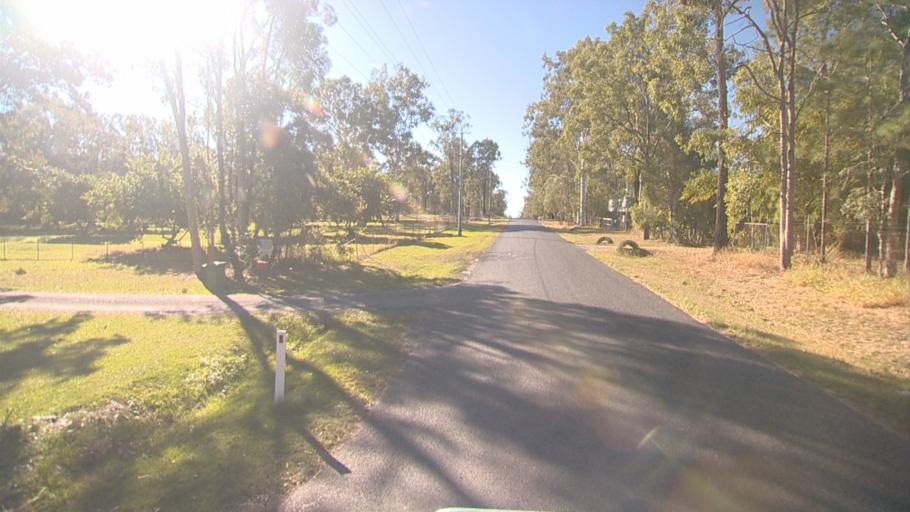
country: AU
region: Queensland
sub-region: Logan
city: Park Ridge South
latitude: -27.7292
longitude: 153.0117
